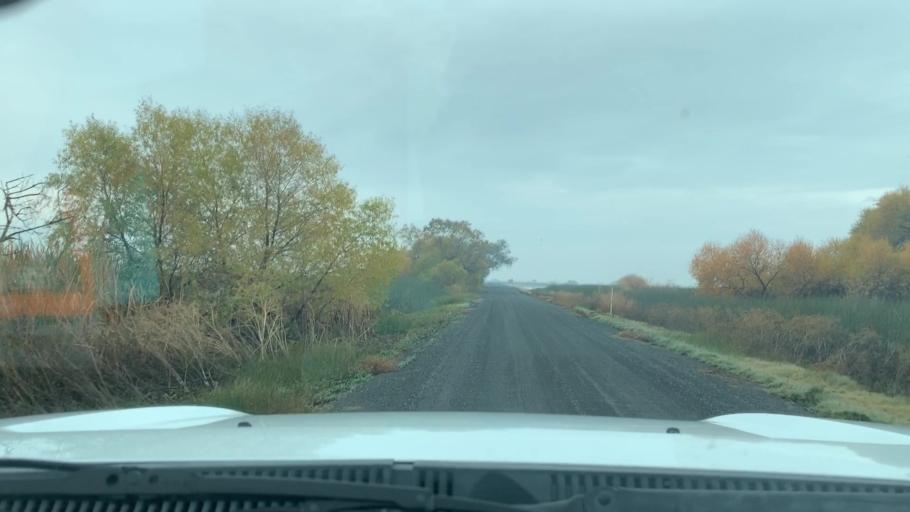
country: US
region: California
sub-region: Kern County
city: Lost Hills
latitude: 35.7336
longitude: -119.6025
